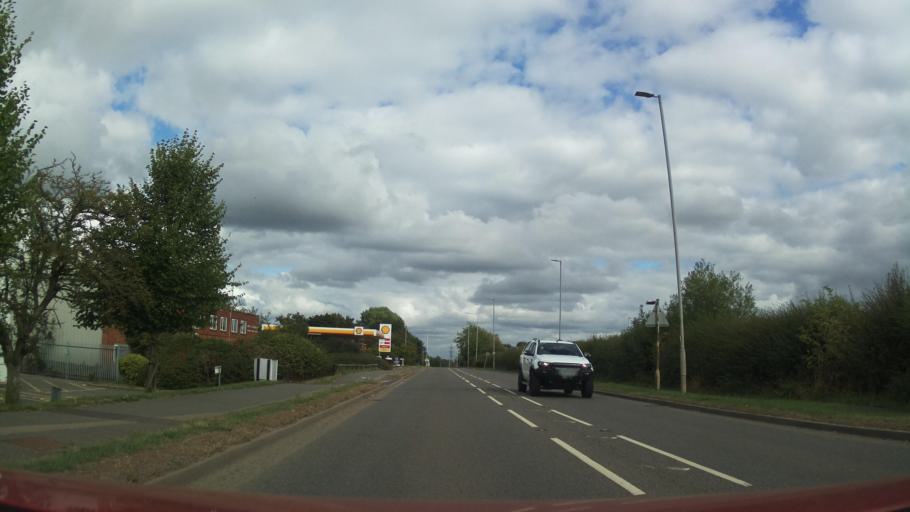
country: GB
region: England
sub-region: Leicestershire
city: Shepshed
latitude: 52.7600
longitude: -1.2952
